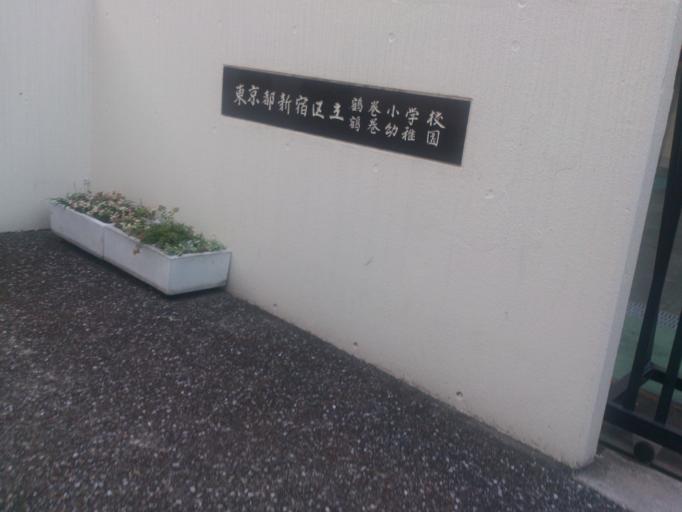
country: JP
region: Tokyo
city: Tokyo
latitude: 35.7086
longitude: 139.7245
